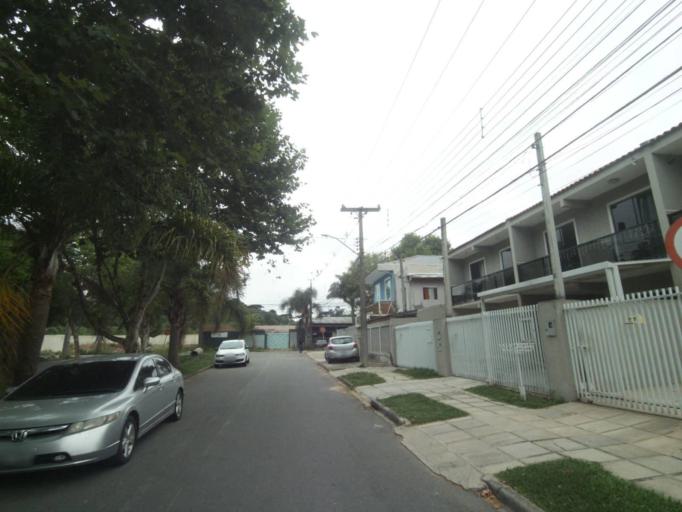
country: BR
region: Parana
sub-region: Araucaria
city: Araucaria
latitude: -25.5503
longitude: -49.3384
